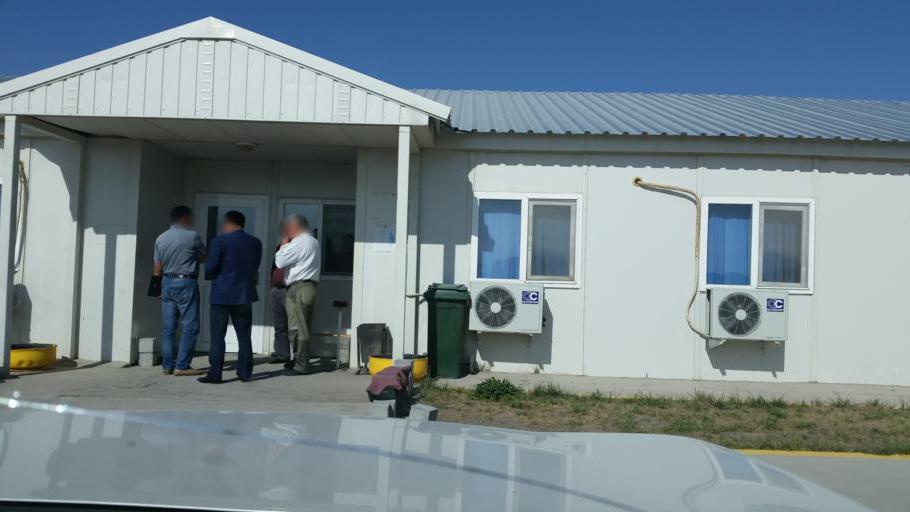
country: KZ
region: Almaty Oblysy
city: Turgen'
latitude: 43.5233
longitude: 77.5644
